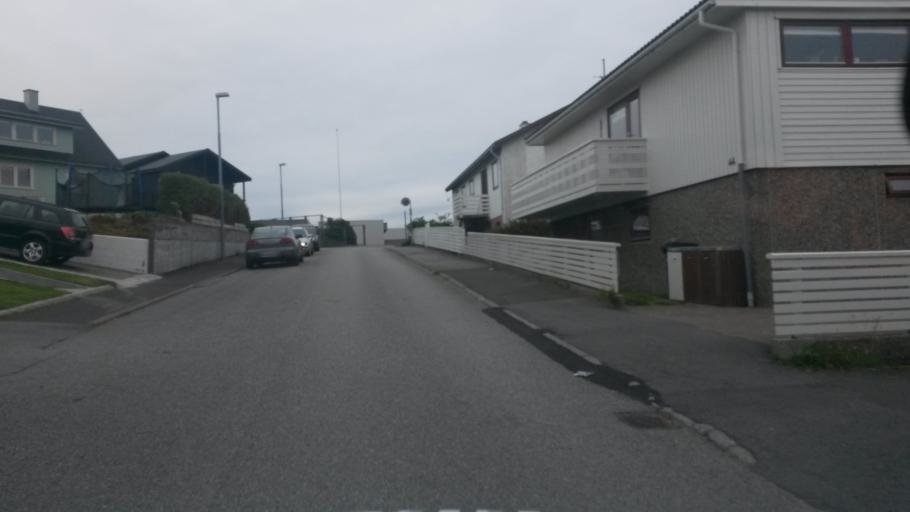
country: FO
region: Streymoy
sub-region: Torshavn
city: Torshavn
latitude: 62.0127
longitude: -6.7633
